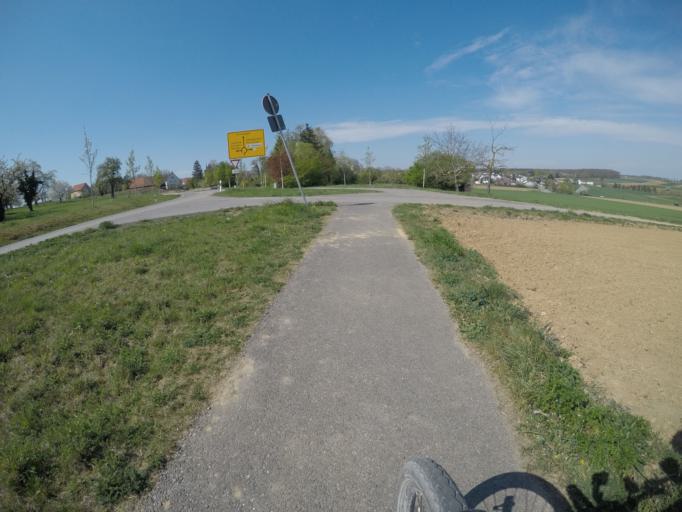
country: DE
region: Baden-Wuerttemberg
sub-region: Regierungsbezirk Stuttgart
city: Hemmingen
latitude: 48.8467
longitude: 9.0355
